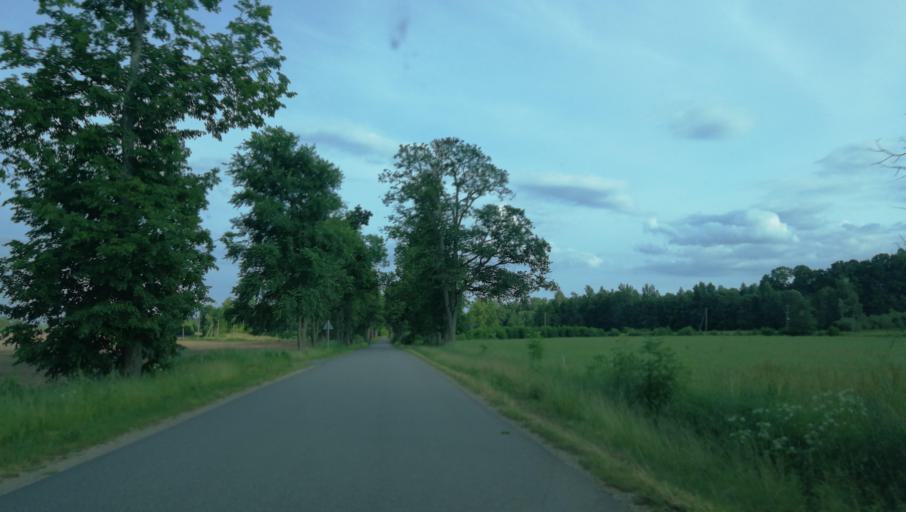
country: LV
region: Pargaujas
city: Stalbe
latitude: 57.3574
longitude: 25.0897
